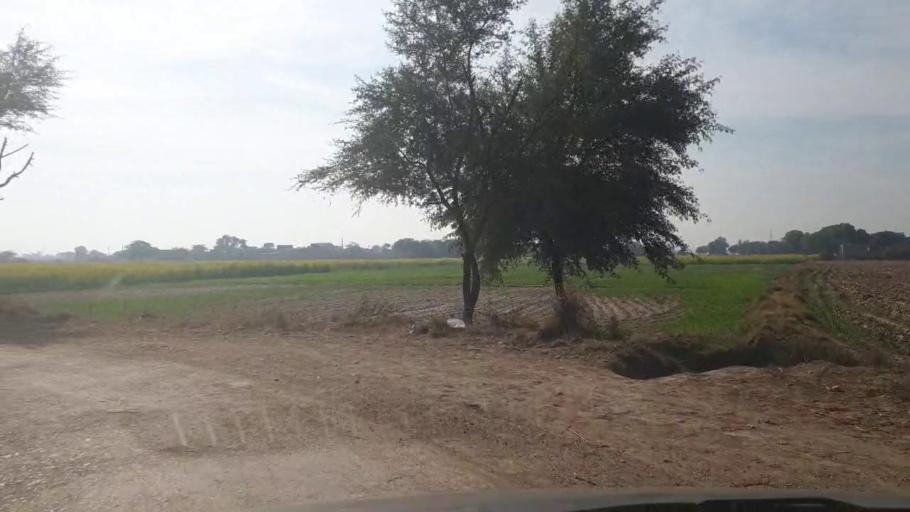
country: PK
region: Sindh
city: Shahpur Chakar
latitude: 26.1765
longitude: 68.5839
